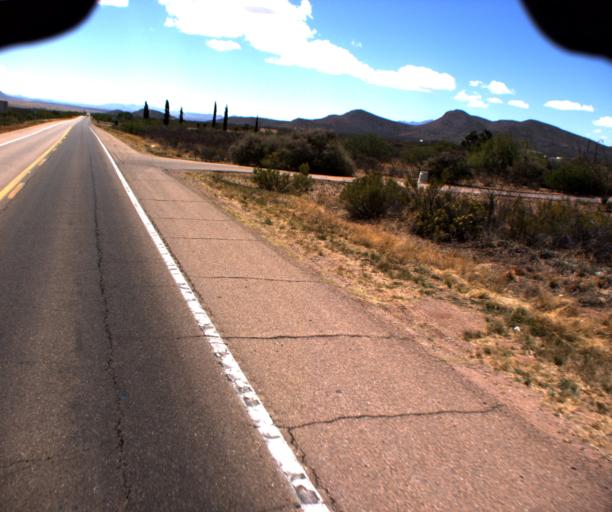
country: US
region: Arizona
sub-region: Cochise County
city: Bisbee
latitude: 31.3945
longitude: -109.9334
